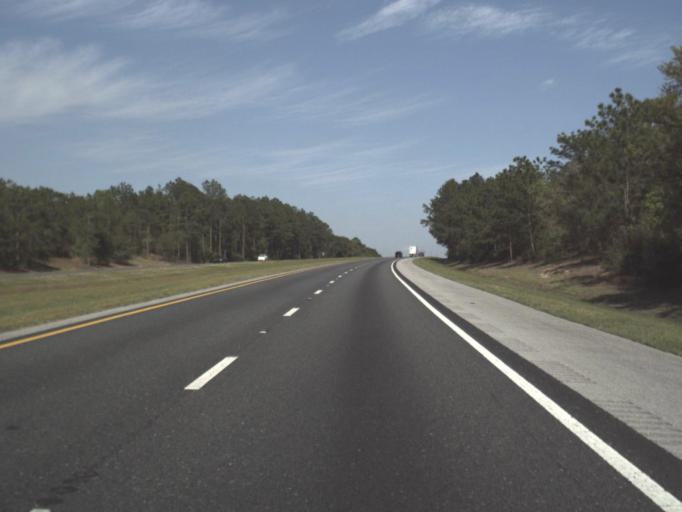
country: US
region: Florida
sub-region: Okaloosa County
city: Crestview
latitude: 30.7142
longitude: -86.6919
